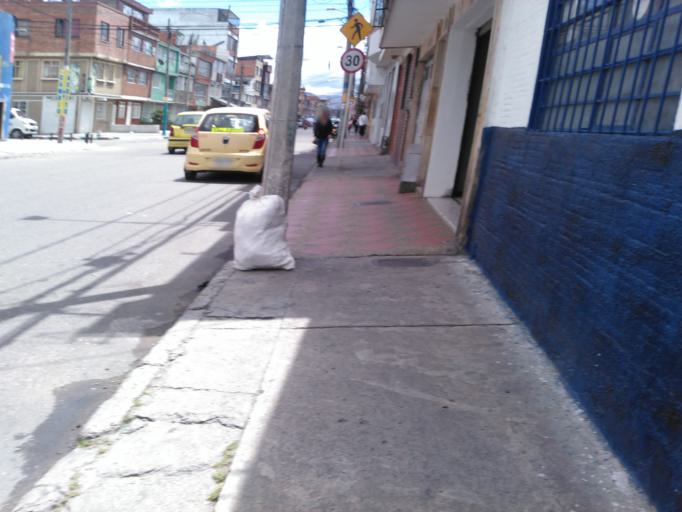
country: CO
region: Bogota D.C.
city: Bogota
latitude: 4.6256
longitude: -74.1146
